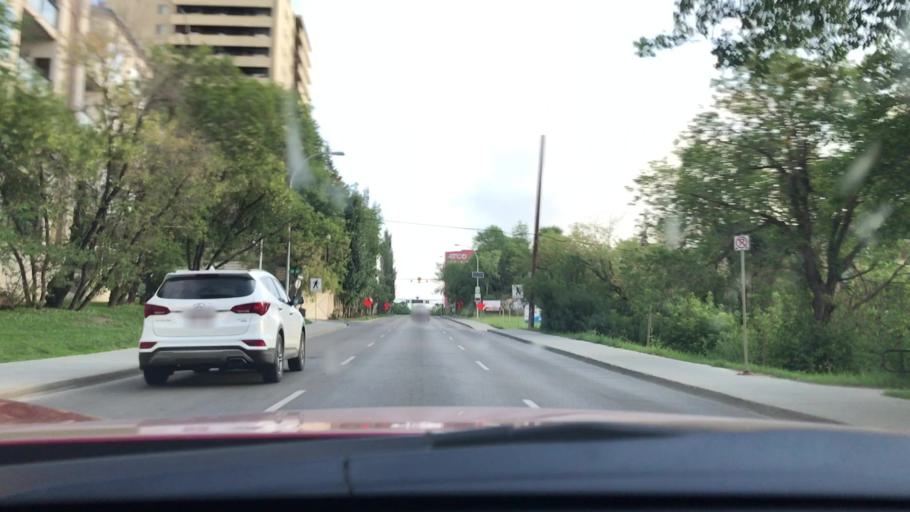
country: CA
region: Alberta
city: Edmonton
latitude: 53.5351
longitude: -113.5011
